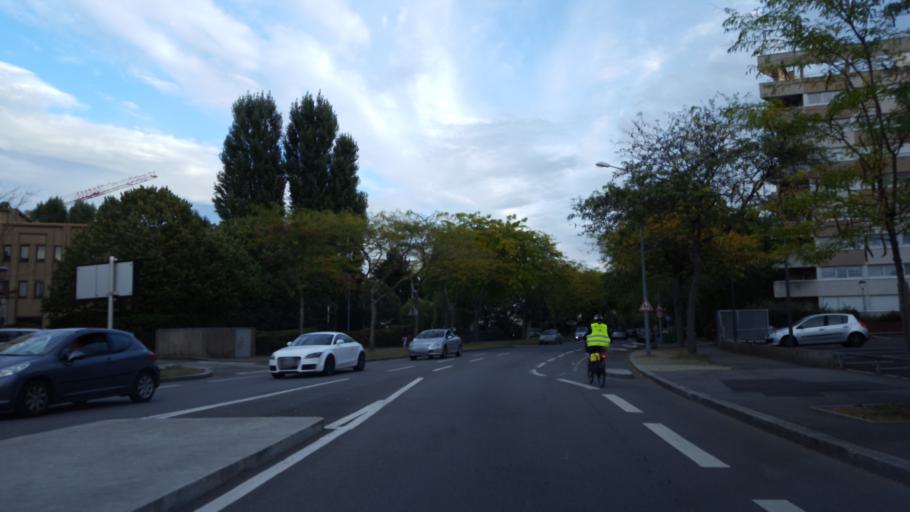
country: FR
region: Pays de la Loire
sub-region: Departement de la Loire-Atlantique
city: Nantes
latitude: 47.2078
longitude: -1.5302
